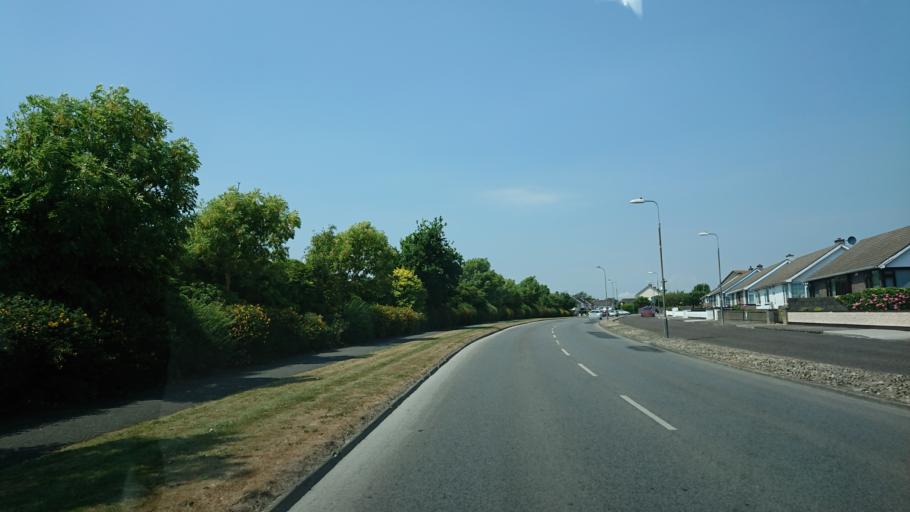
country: IE
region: Munster
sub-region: Waterford
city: Waterford
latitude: 52.2474
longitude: -7.1388
